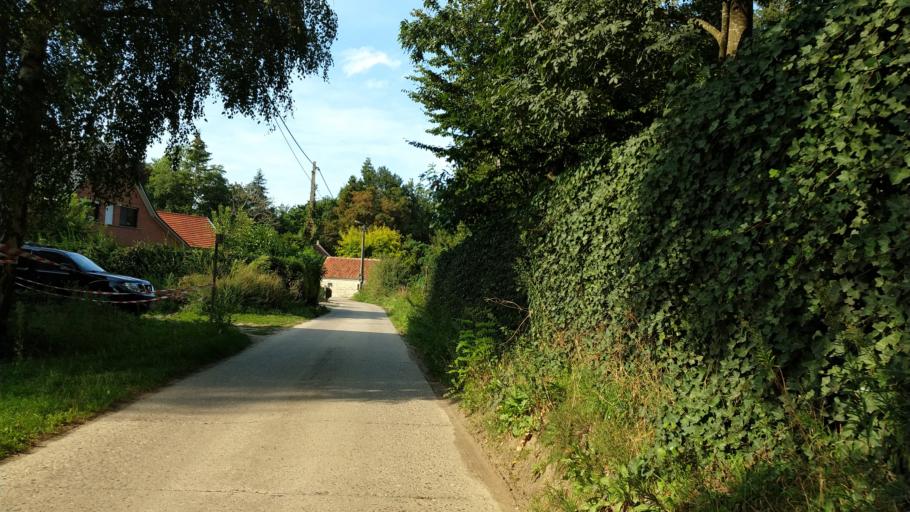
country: BE
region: Flanders
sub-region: Provincie Vlaams-Brabant
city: Lubbeek
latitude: 50.8618
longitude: 4.8217
